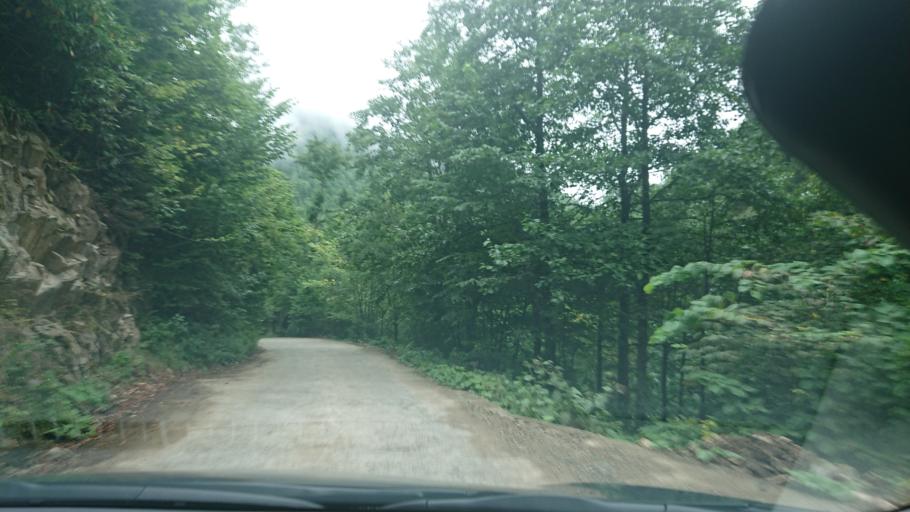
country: TR
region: Gumushane
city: Kurtun
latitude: 40.6725
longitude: 39.0436
